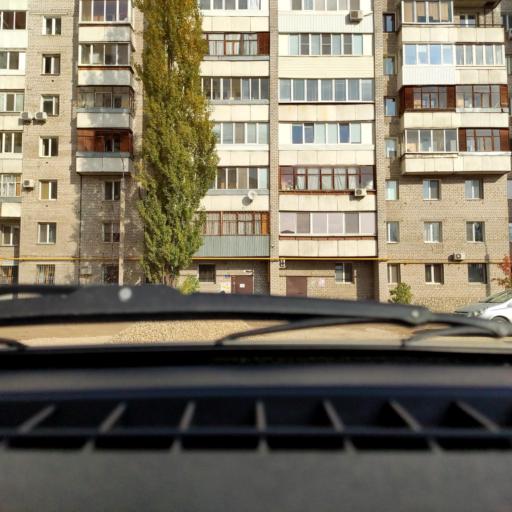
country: RU
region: Bashkortostan
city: Ufa
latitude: 54.7453
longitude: 56.0004
